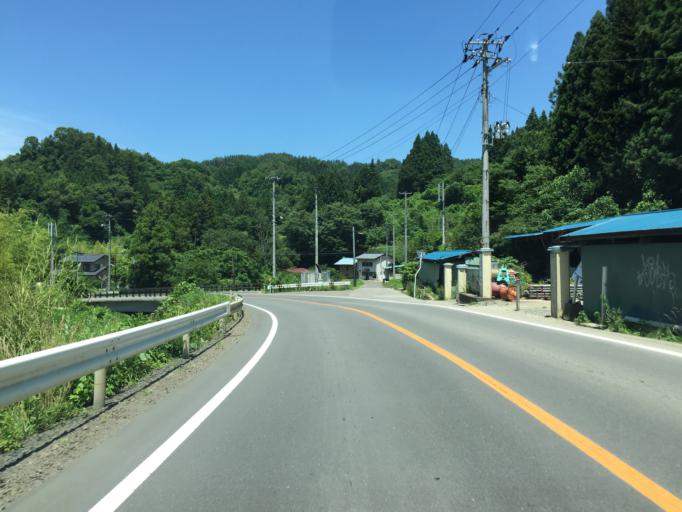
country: JP
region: Fukushima
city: Yanagawamachi-saiwaicho
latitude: 37.7587
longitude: 140.6624
